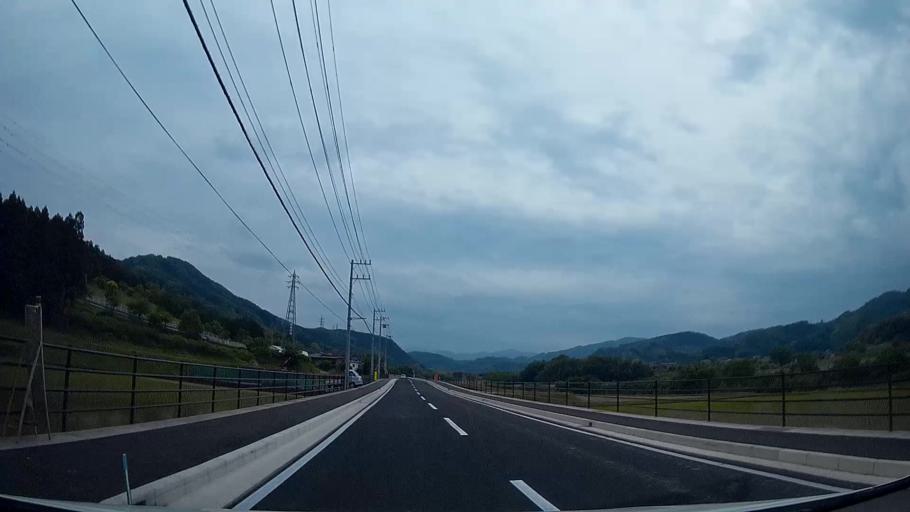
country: JP
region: Shizuoka
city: Ito
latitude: 34.9564
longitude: 138.9438
